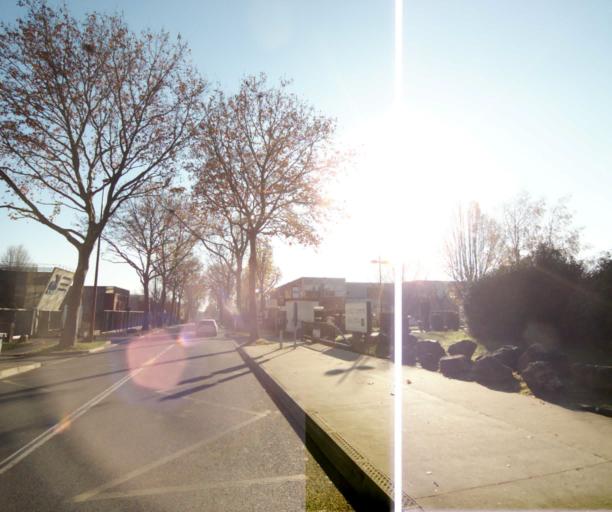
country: FR
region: Ile-de-France
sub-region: Departement du Val-d'Oise
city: Gonesse
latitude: 48.9917
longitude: 2.4328
